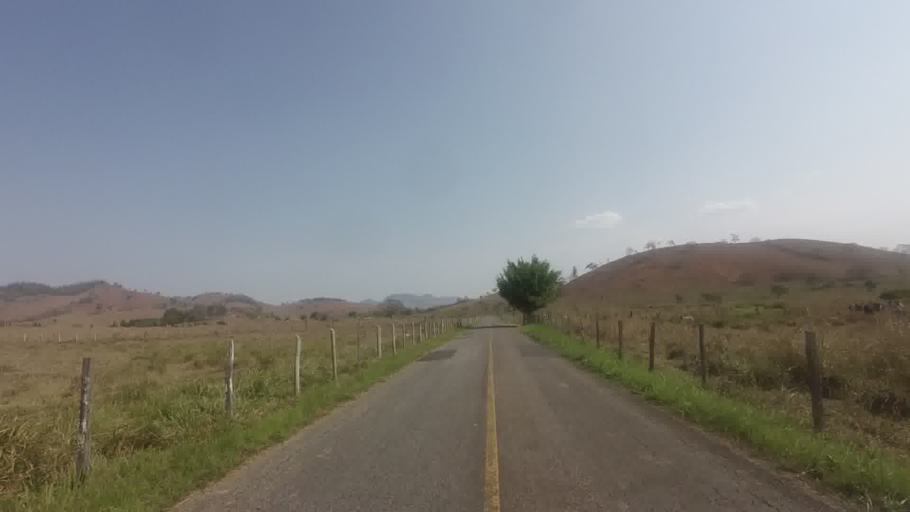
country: BR
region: Rio de Janeiro
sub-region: Bom Jesus Do Itabapoana
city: Bom Jesus do Itabapoana
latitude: -21.1296
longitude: -41.5675
